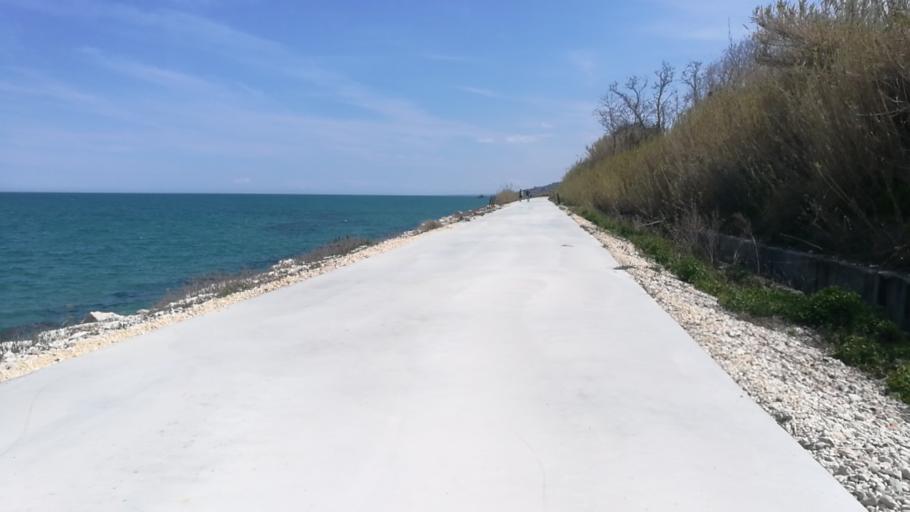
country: IT
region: Abruzzo
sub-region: Provincia di Chieti
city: Marina di San Vito
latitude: 42.3237
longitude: 14.4279
